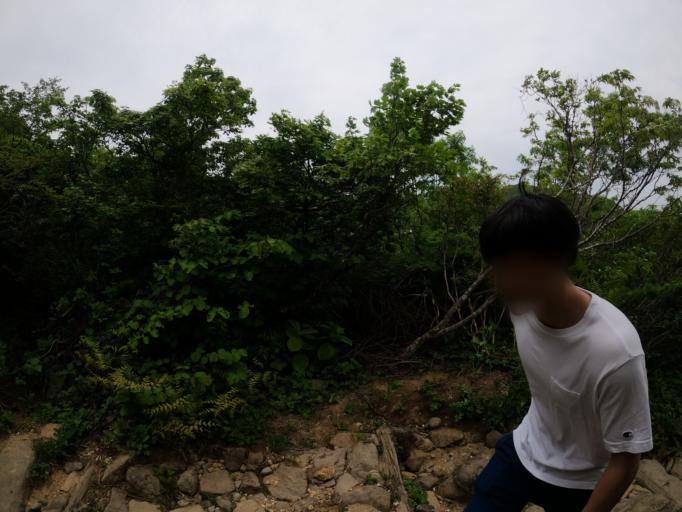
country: JP
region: Akita
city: Yuzawa
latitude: 38.9722
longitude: 140.7857
